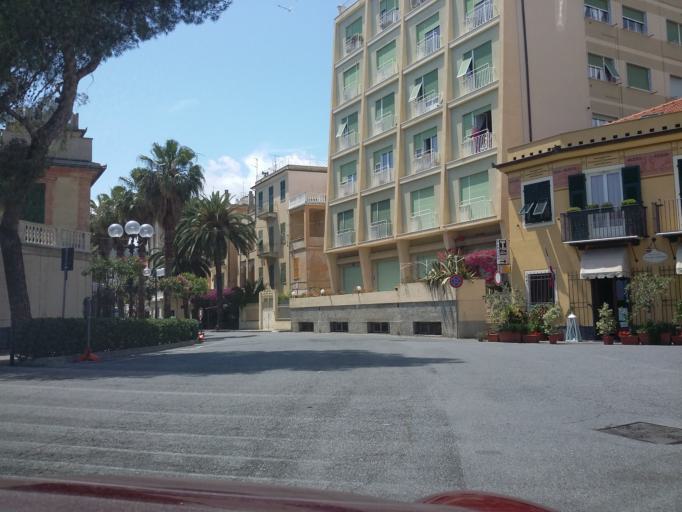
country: IT
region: Liguria
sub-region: Provincia di Savona
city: Spotorno
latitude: 44.2281
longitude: 8.4205
